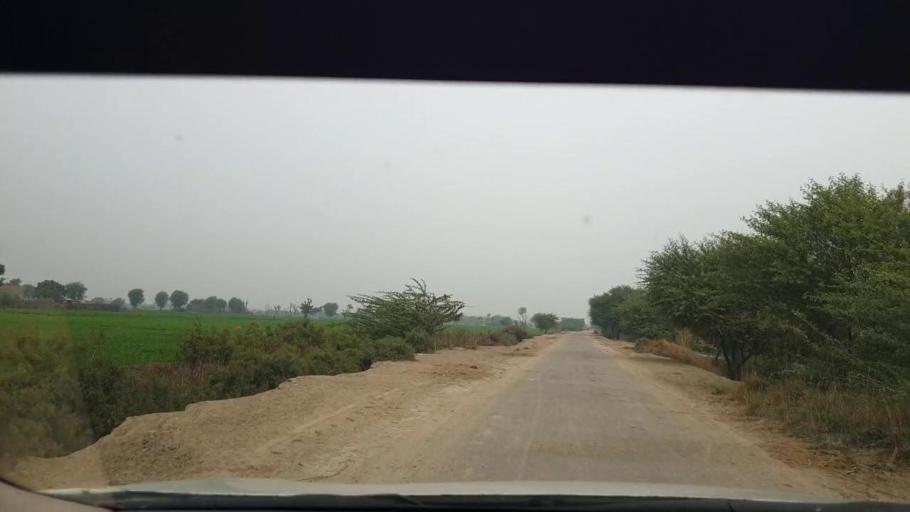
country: PK
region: Sindh
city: Berani
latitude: 25.8688
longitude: 68.8263
